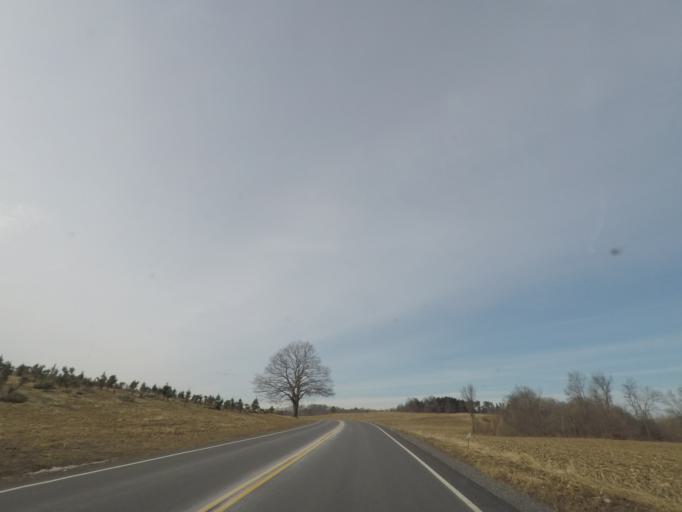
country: US
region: New York
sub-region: Columbia County
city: Valatie
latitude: 42.3973
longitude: -73.6526
